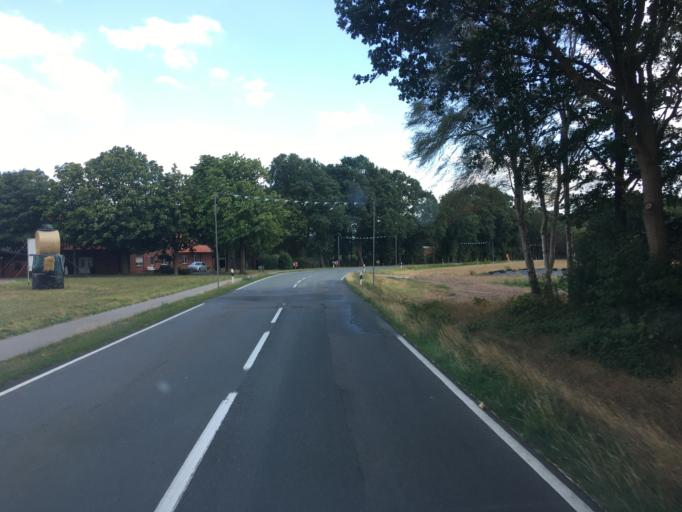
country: DE
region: Lower Saxony
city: Friesoythe
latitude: 53.0769
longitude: 7.8431
